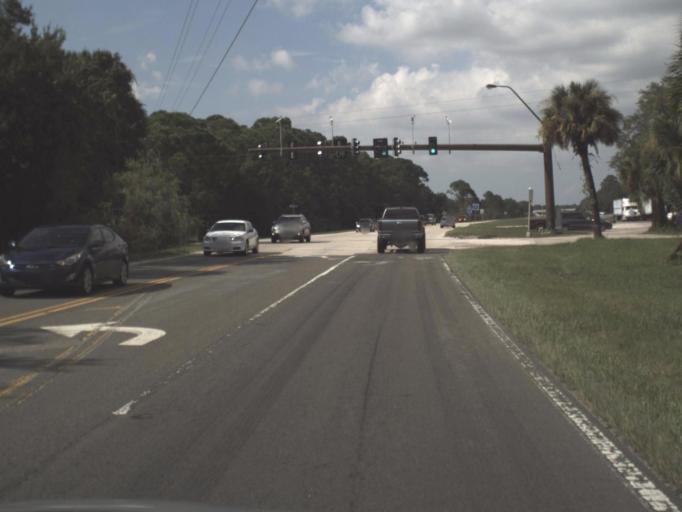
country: US
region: Florida
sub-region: Sarasota County
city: Plantation
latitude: 27.0988
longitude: -82.3435
